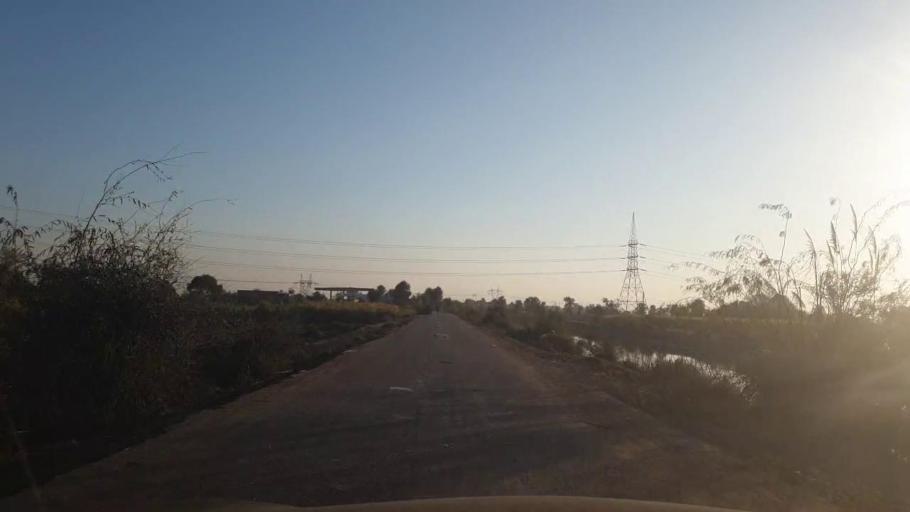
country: PK
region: Sindh
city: Mirpur Mathelo
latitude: 27.9911
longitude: 69.4653
